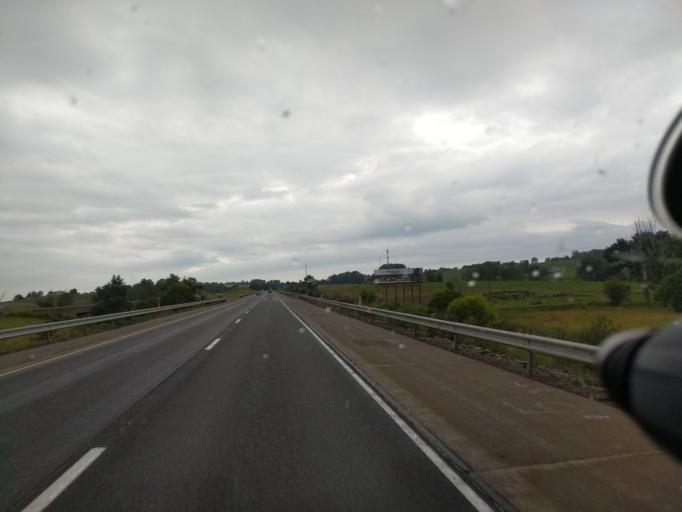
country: US
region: Pennsylvania
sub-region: Northumberland County
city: Milton
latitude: 41.0097
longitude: -76.7738
